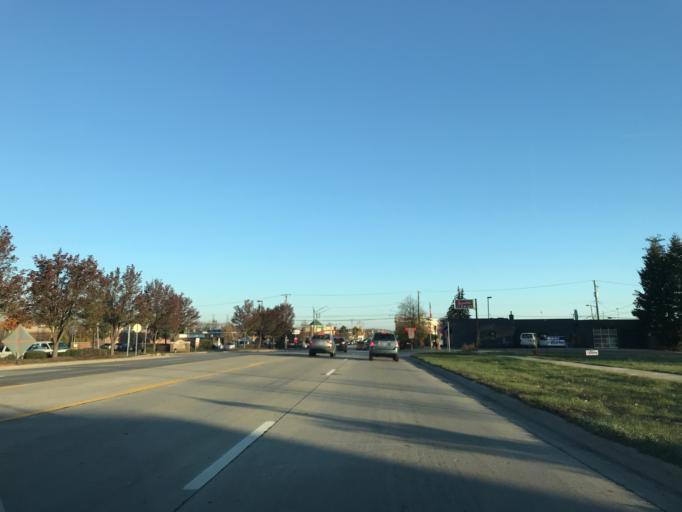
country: US
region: Michigan
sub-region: Oakland County
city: Novi
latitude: 42.4791
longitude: -83.4754
